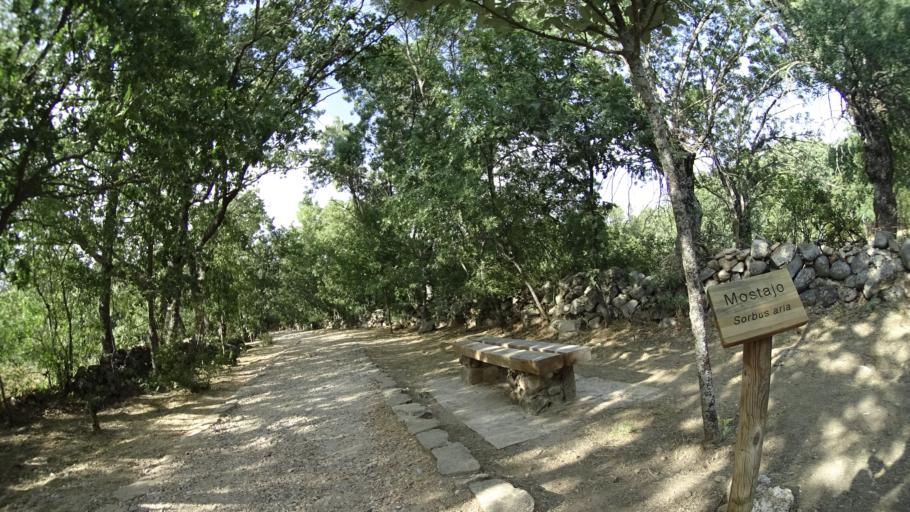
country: ES
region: Madrid
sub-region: Provincia de Madrid
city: Navacerrada
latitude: 40.7242
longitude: -4.0032
